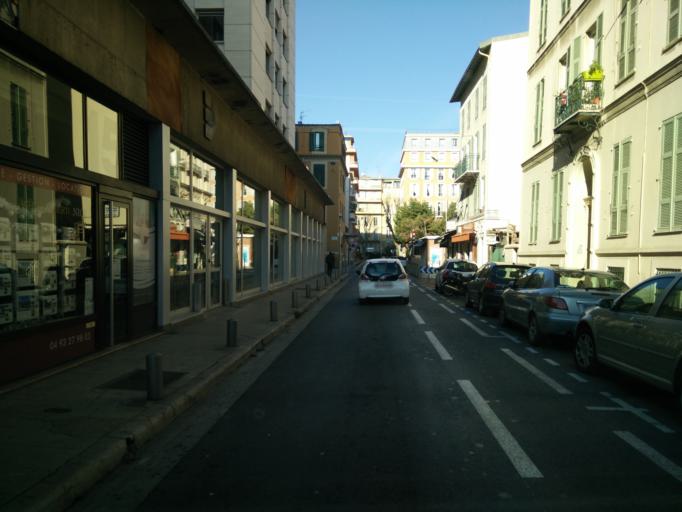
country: FR
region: Provence-Alpes-Cote d'Azur
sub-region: Departement des Alpes-Maritimes
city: Nice
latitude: 43.7003
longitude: 7.2714
